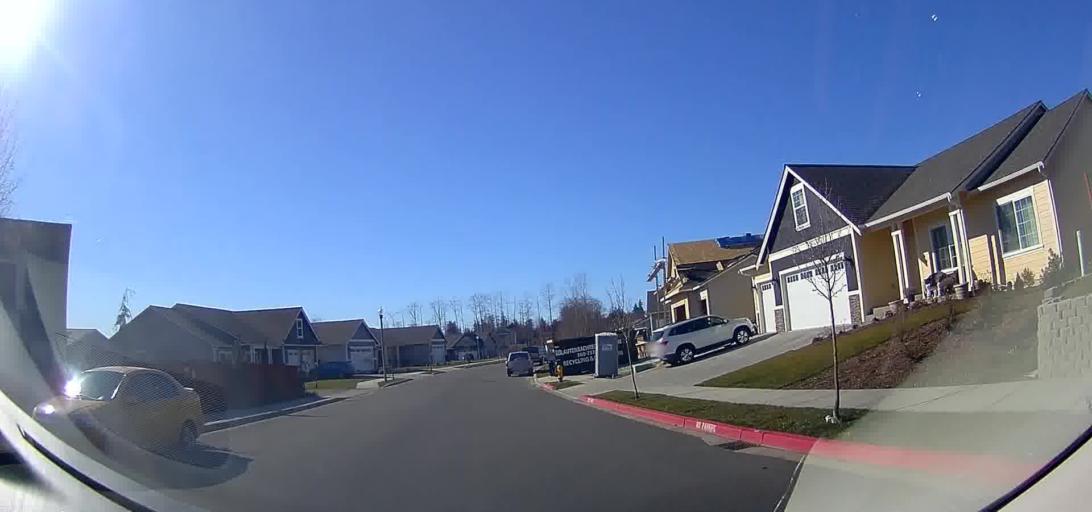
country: US
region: Washington
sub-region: Skagit County
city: Mount Vernon
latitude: 48.4401
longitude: -122.2976
